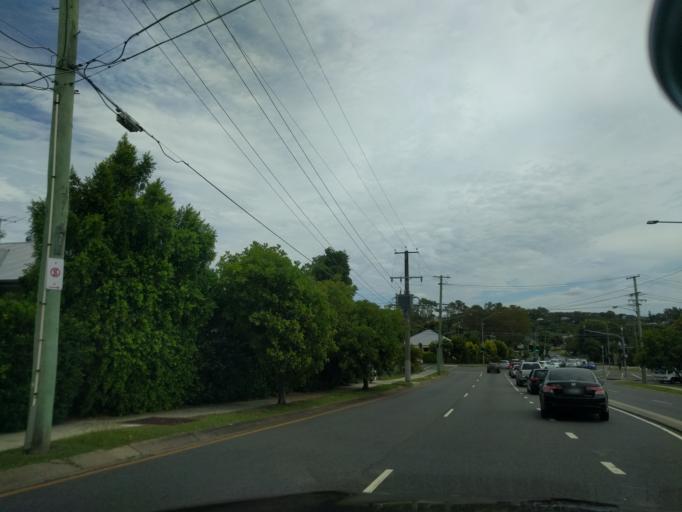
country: AU
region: Queensland
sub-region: Brisbane
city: Stafford
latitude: -27.4101
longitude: 153.0076
